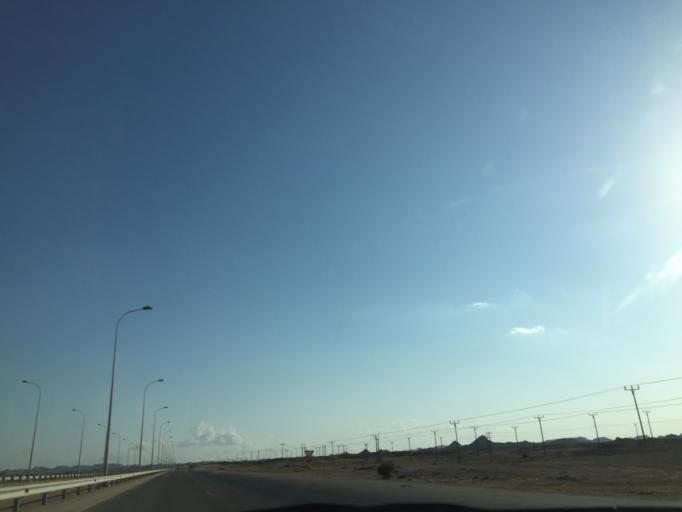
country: OM
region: Zufar
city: Salalah
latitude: 17.5283
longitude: 54.0558
